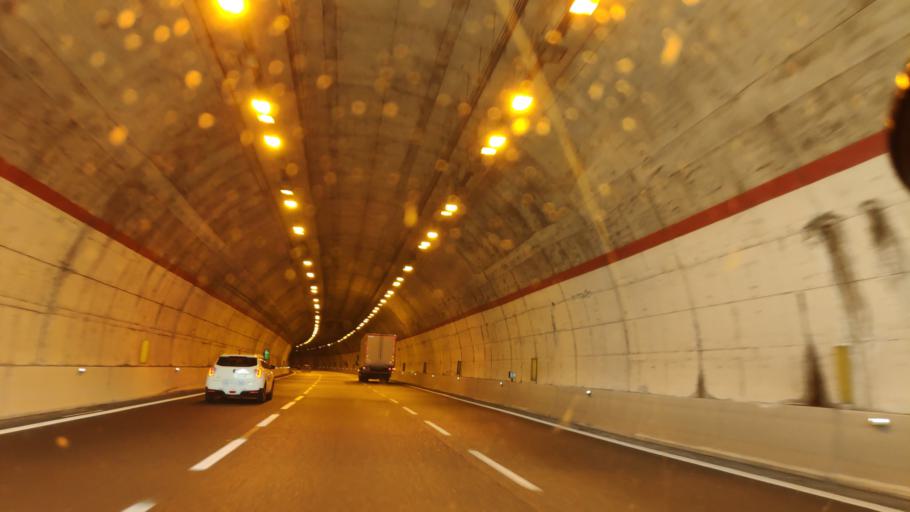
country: IT
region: Campania
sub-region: Provincia di Salerno
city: Contursi Terme
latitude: 40.6174
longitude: 15.2446
